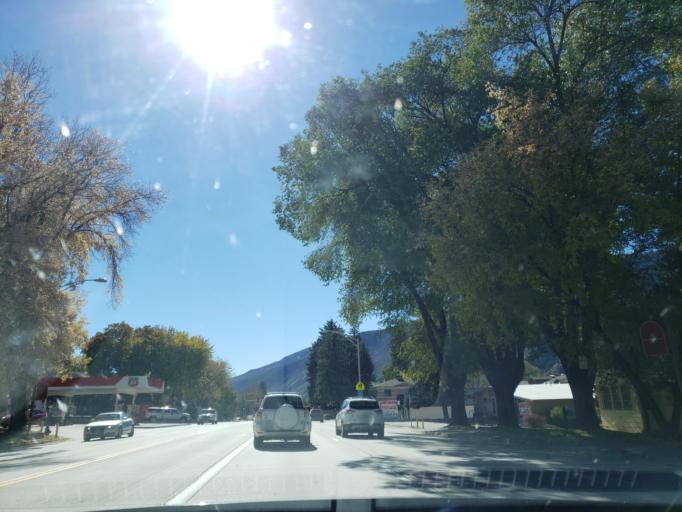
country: US
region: Colorado
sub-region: Garfield County
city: Glenwood Springs
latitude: 39.5408
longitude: -107.3250
